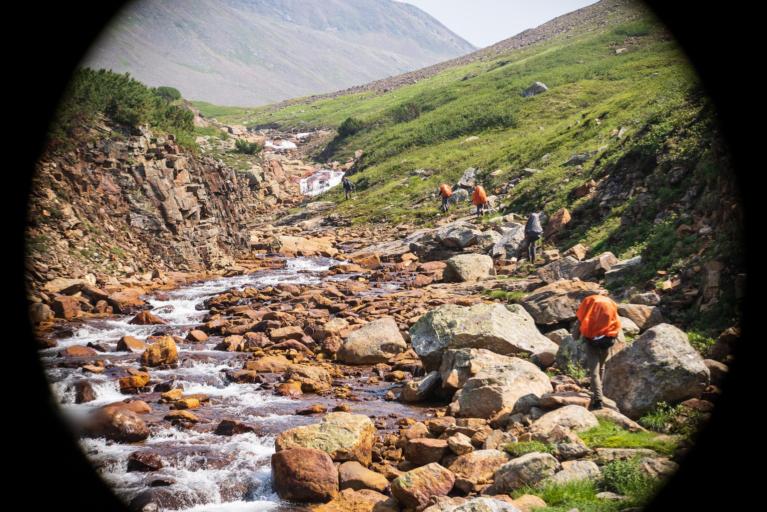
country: RU
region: Transbaikal Territory
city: Kuanda
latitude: 56.8094
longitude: 116.9095
